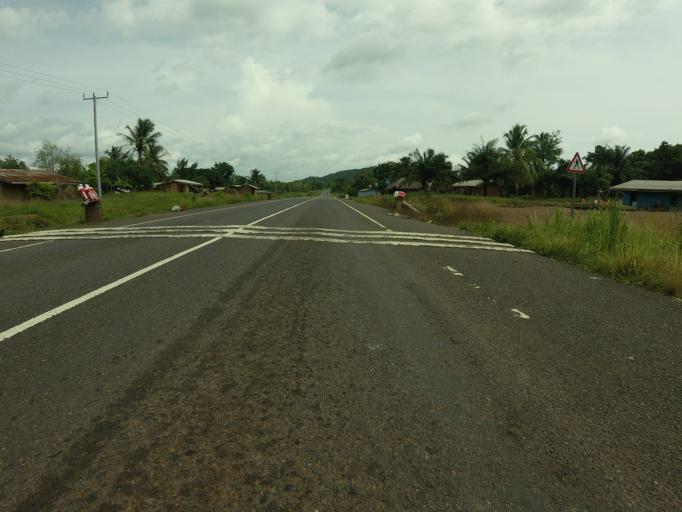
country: TG
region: Plateaux
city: Badou
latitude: 7.9531
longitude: 0.5546
